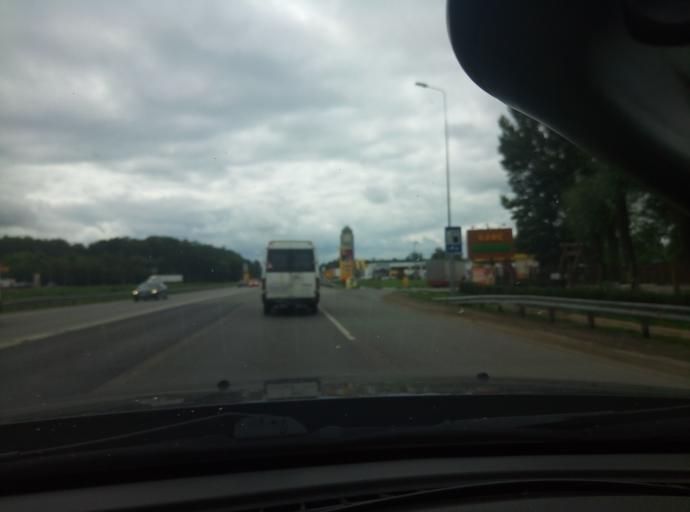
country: RU
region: Kaluga
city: Obninsk
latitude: 55.1066
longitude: 36.6419
